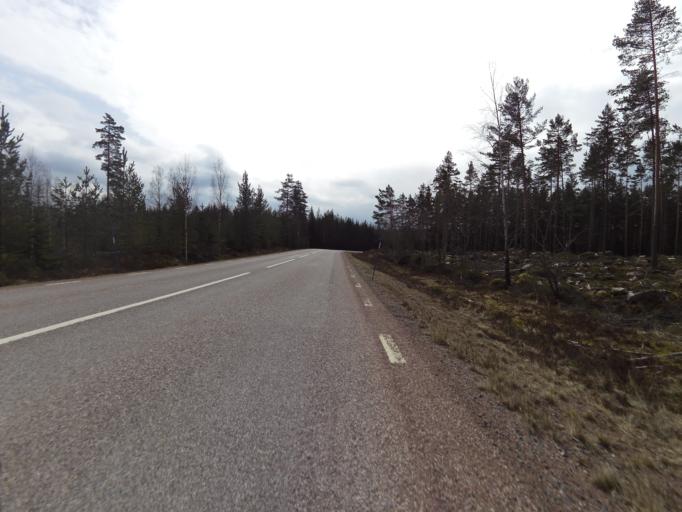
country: SE
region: Dalarna
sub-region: Hedemora Kommun
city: Langshyttan
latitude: 60.5224
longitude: 16.1365
